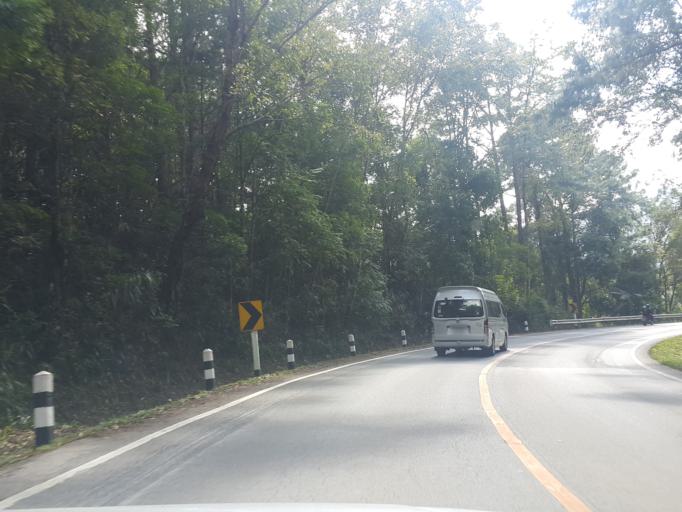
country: TH
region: Chiang Mai
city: Mae Chaem
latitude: 18.5410
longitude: 98.5305
